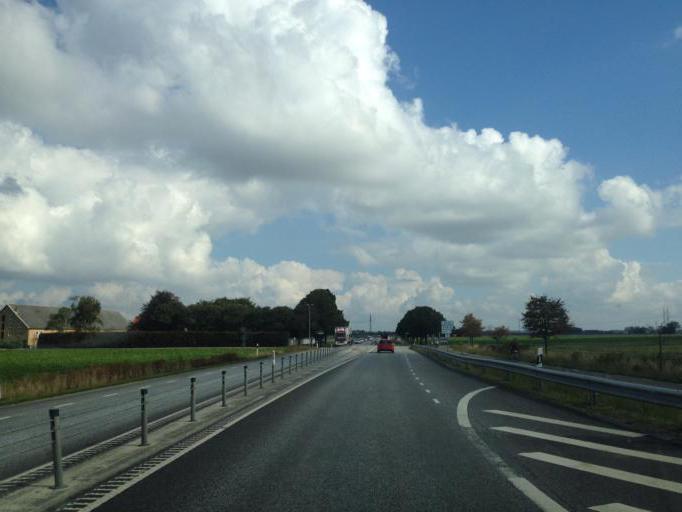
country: SE
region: Skane
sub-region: Lomma Kommun
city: Lomma
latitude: 55.6875
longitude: 13.1031
